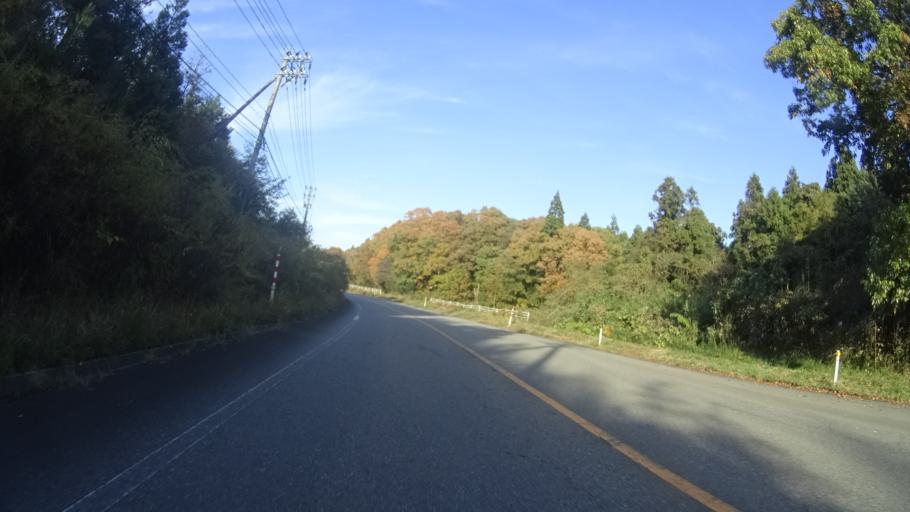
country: JP
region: Ishikawa
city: Hakui
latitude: 37.0508
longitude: 136.7757
